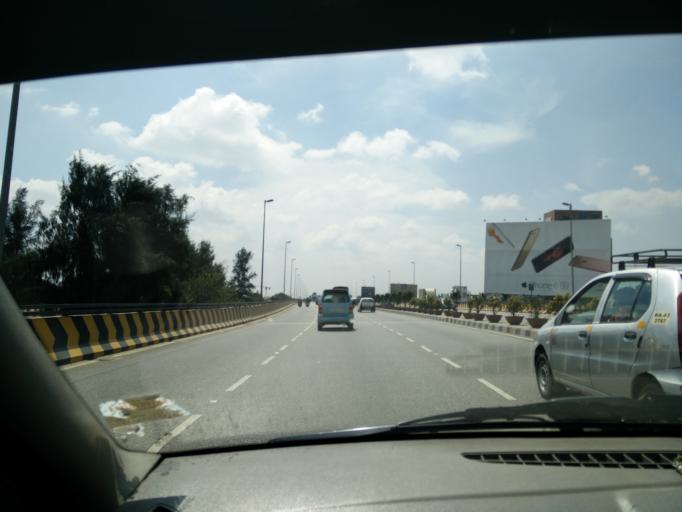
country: IN
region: Karnataka
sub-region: Bangalore Urban
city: Yelahanka
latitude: 13.0819
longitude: 77.5933
